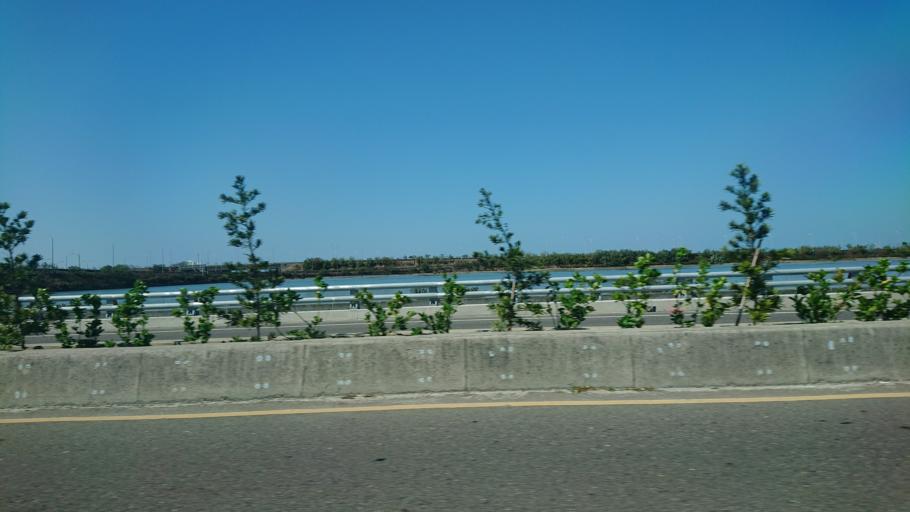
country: TW
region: Taiwan
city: Xinying
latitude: 23.2794
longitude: 120.1308
